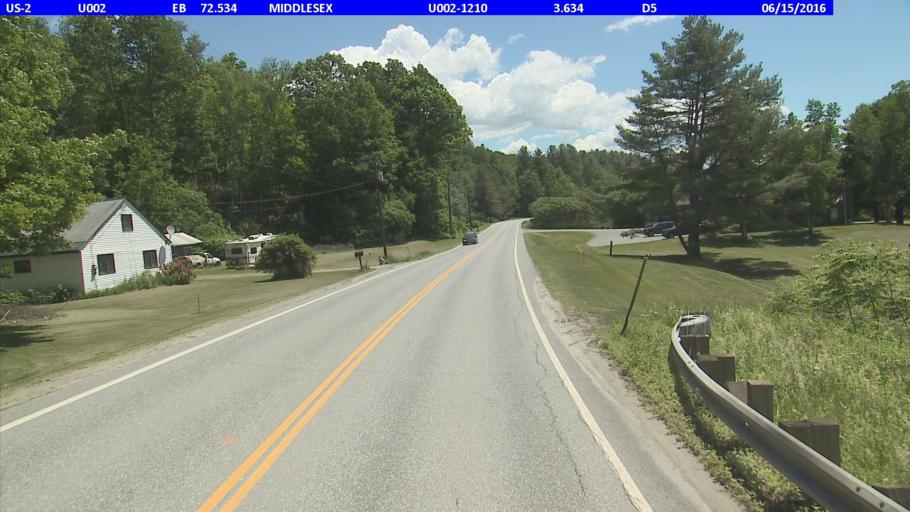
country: US
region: Vermont
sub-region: Washington County
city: Montpelier
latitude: 44.2763
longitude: -72.6440
